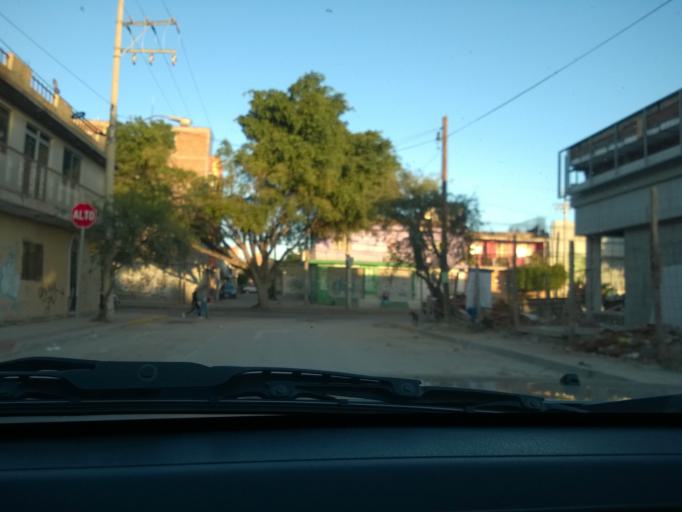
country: MX
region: Guanajuato
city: Leon
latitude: 21.1290
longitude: -101.6601
